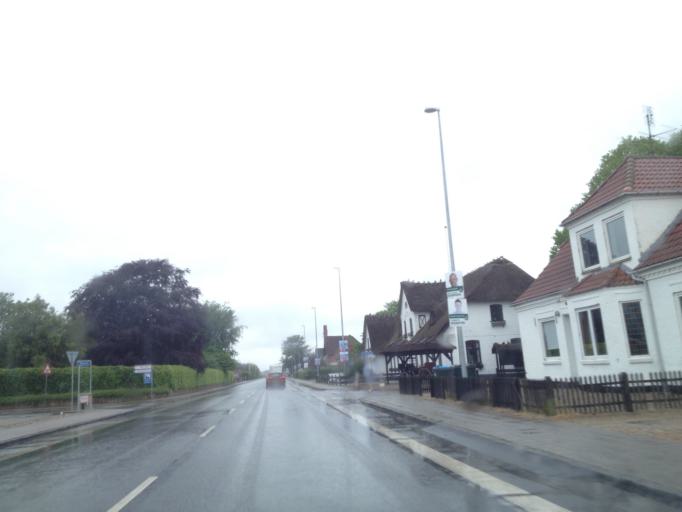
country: DK
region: South Denmark
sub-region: Tonder Kommune
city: Sherrebek
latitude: 55.1168
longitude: 8.8094
